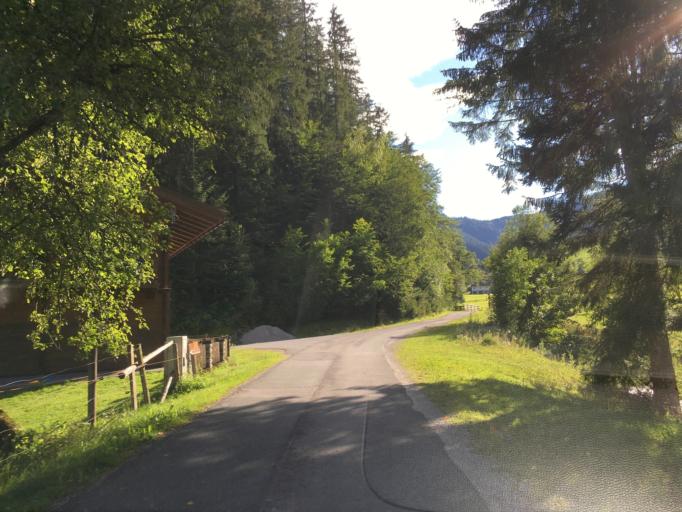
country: AT
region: Salzburg
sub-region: Politischer Bezirk Hallein
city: Abtenau
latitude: 47.4973
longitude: 13.3755
